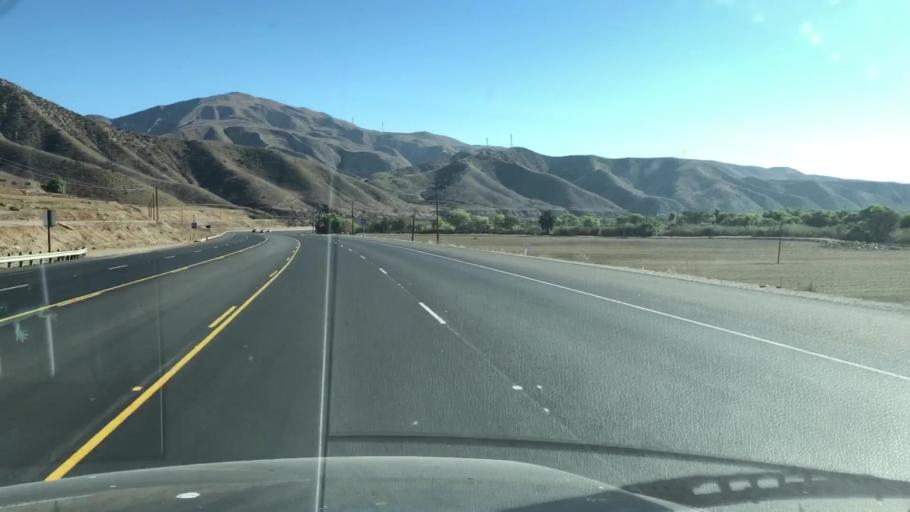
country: US
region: California
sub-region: Ventura County
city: Piru
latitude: 34.4077
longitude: -118.7362
